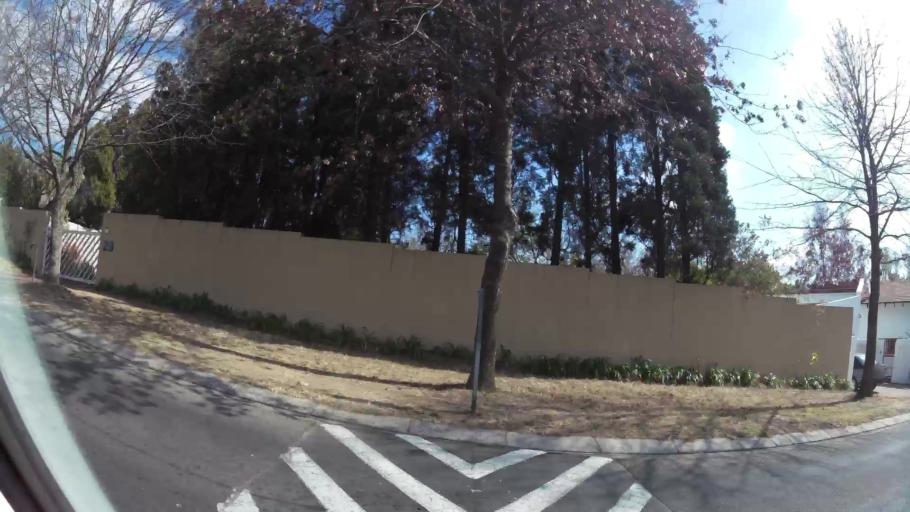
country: ZA
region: Gauteng
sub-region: City of Johannesburg Metropolitan Municipality
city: Midrand
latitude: -26.0289
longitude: 28.0755
